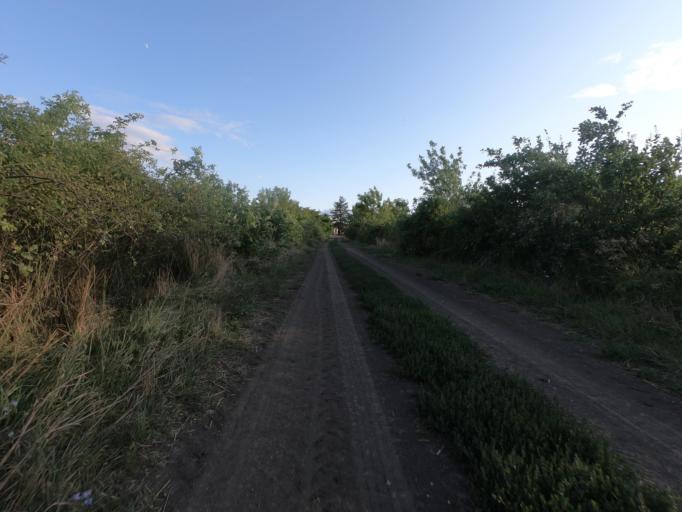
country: HU
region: Heves
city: Szihalom
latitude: 47.7187
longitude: 20.5486
